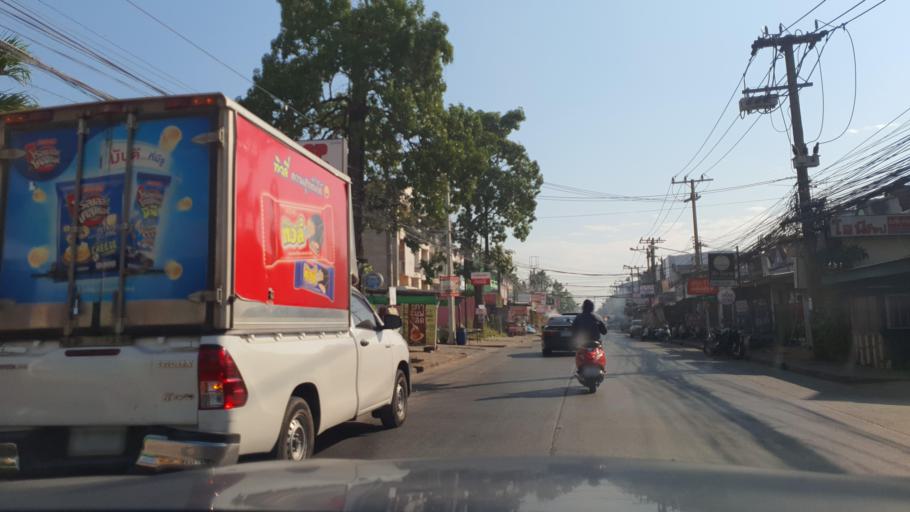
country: TH
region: Khon Kaen
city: Khon Kaen
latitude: 16.4213
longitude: 102.8141
